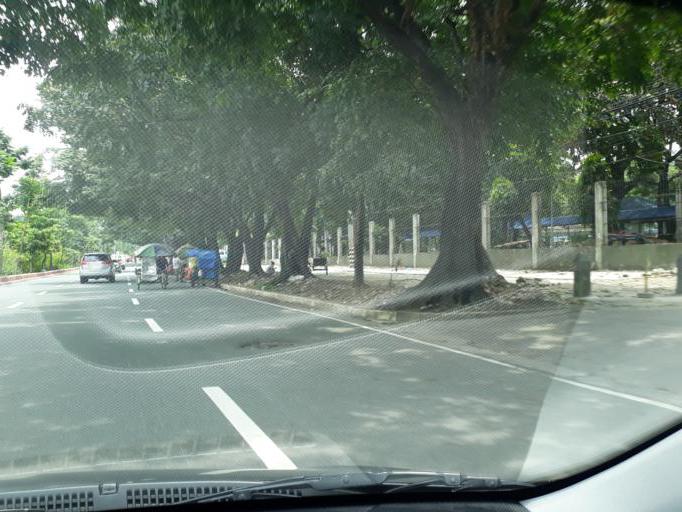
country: PH
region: Metro Manila
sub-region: Quezon City
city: Quezon City
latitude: 14.6501
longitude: 121.0393
